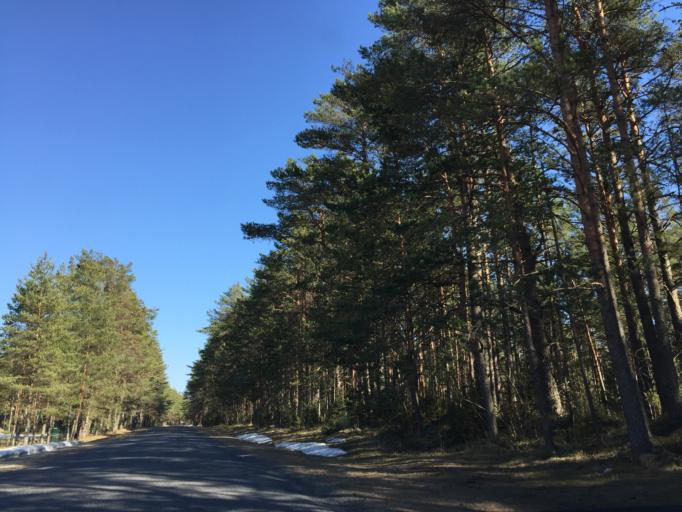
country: EE
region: Ida-Virumaa
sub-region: Johvi vald
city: Johvi
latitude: 59.0095
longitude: 27.4364
